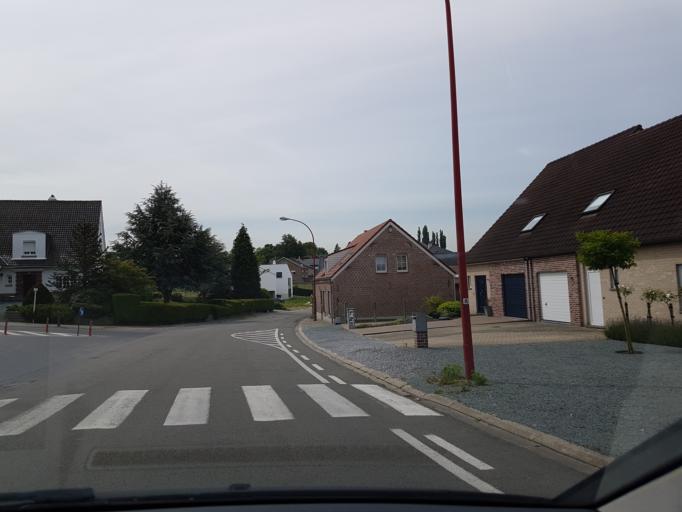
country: BE
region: Flanders
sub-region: Provincie Vlaams-Brabant
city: Asse
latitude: 50.9025
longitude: 4.2058
